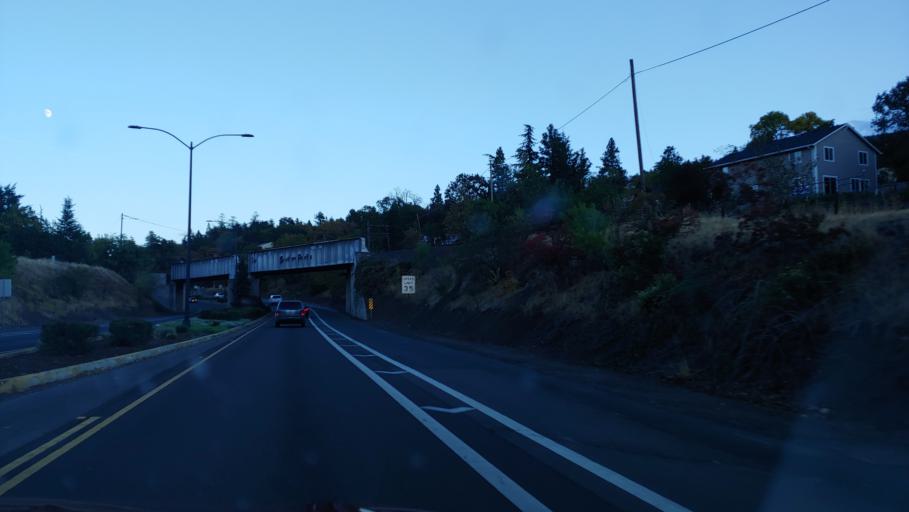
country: US
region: Oregon
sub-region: Jackson County
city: Ashland
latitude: 42.2144
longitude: -122.7312
